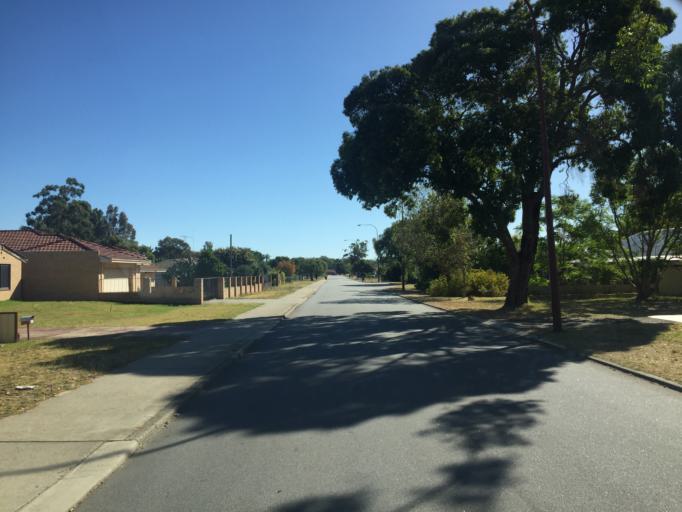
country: AU
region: Western Australia
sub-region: Gosnells
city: Maddington
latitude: -32.0577
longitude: 115.9997
